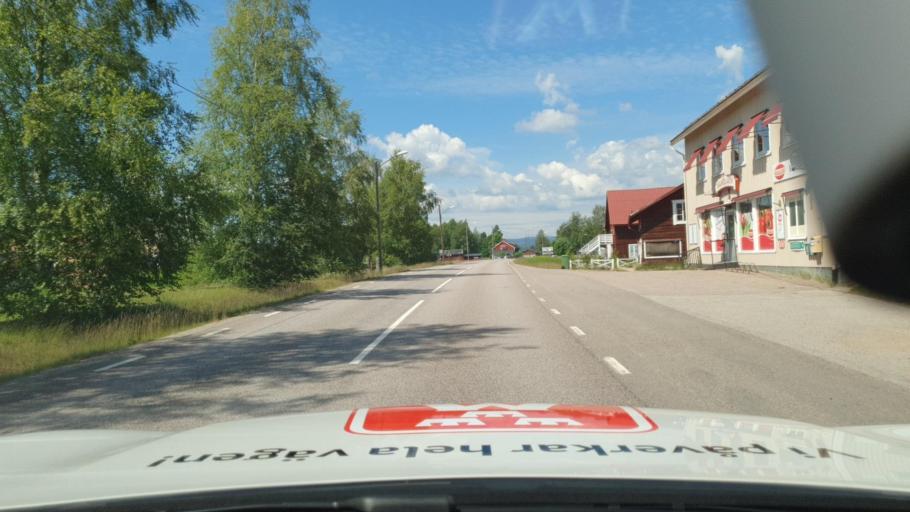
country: SE
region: Vaermland
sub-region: Torsby Kommun
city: Torsby
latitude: 60.3429
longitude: 12.9795
